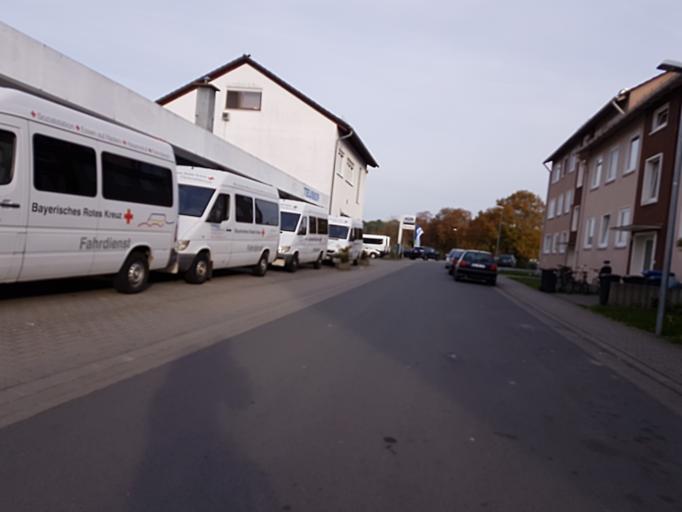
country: DE
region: Bavaria
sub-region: Regierungsbezirk Unterfranken
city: Worth am Main
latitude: 49.8108
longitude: 9.1436
